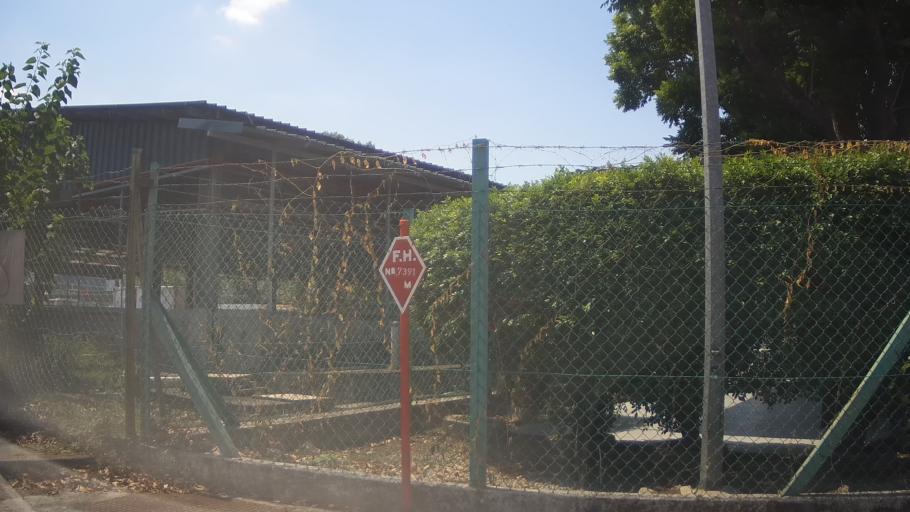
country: SG
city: Singapore
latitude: 1.3144
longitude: 103.7262
